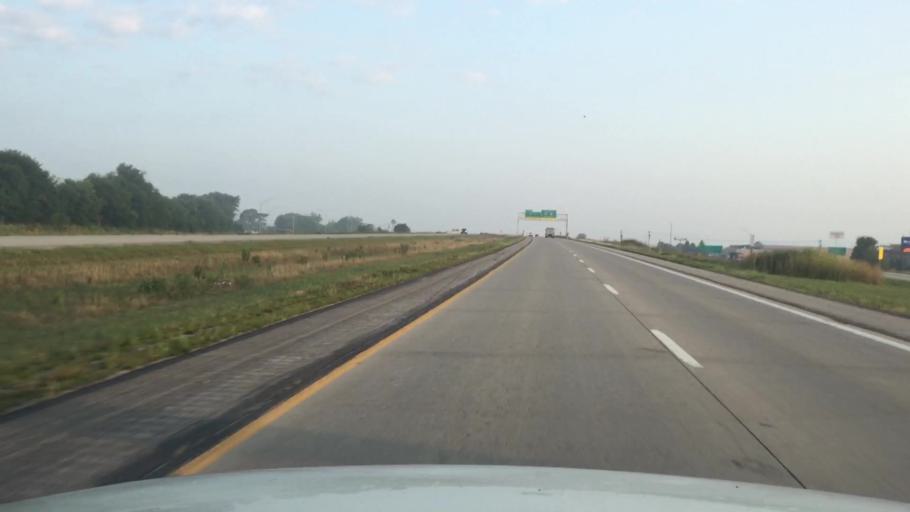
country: US
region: Iowa
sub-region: Polk County
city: Altoona
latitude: 41.6412
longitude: -93.5082
